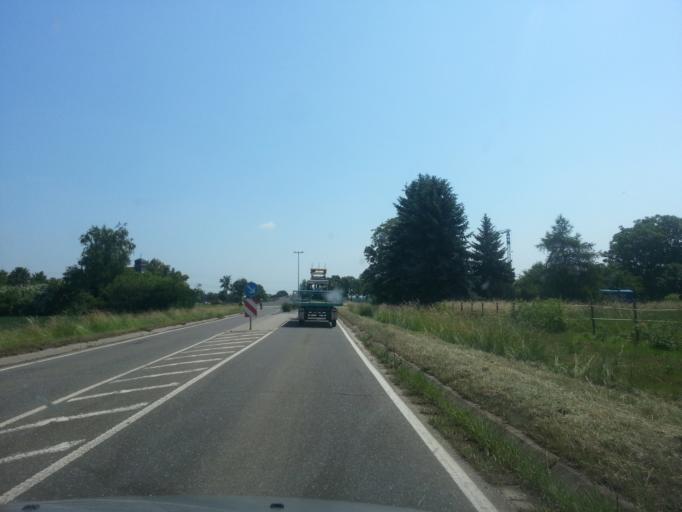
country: DE
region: Rheinland-Pfalz
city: Lambsheim
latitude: 49.5193
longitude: 8.2855
